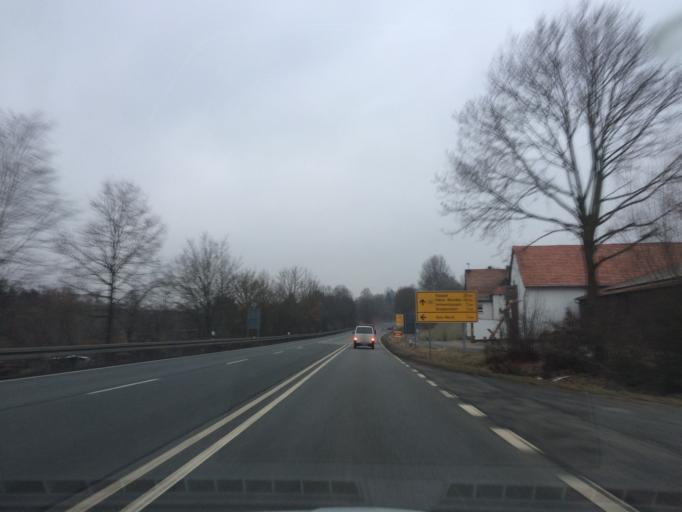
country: DE
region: Hesse
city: Grebenstein
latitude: 51.4564
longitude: 9.4094
